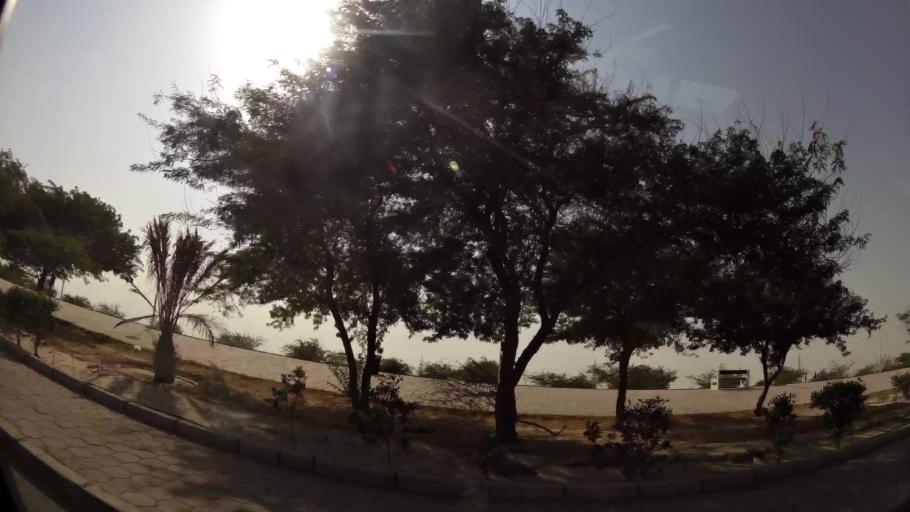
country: KW
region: Muhafazat al Jahra'
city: Al Jahra'
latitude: 29.3255
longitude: 47.6476
